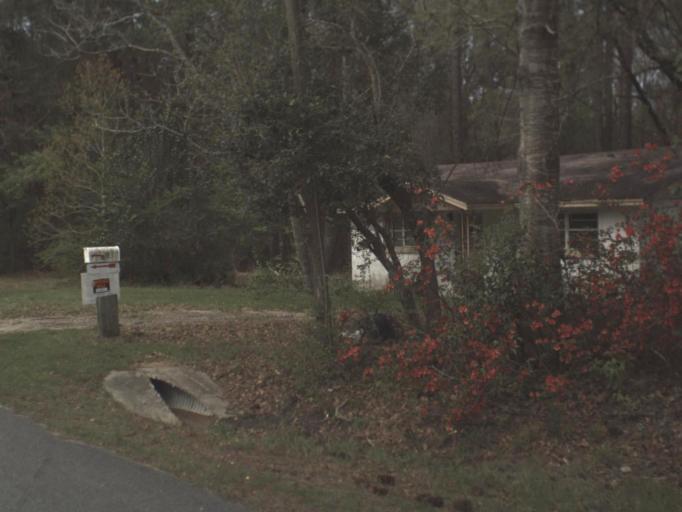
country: US
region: Florida
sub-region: Holmes County
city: Bonifay
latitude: 30.8184
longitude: -85.6709
